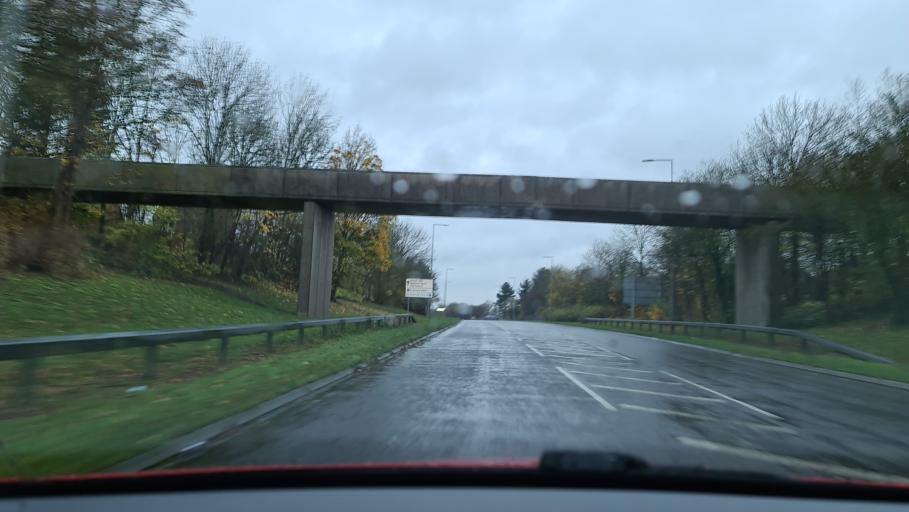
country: GB
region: England
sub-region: Milton Keynes
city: Milton Keynes
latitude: 52.0537
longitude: -0.7399
